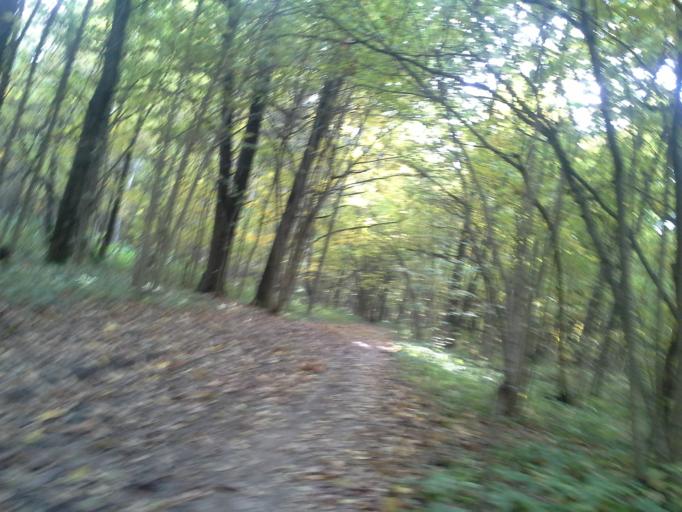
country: RU
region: Moskovskaya
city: Kommunarka
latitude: 55.5620
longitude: 37.5199
